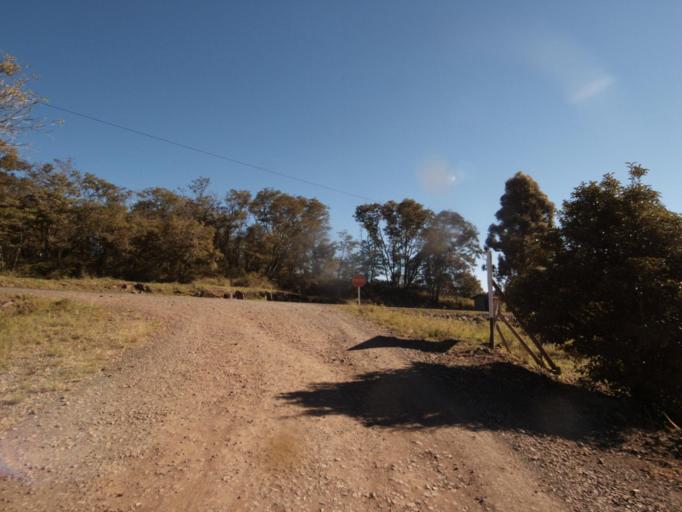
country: AR
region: Misiones
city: Bernardo de Irigoyen
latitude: -26.6778
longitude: -53.5602
